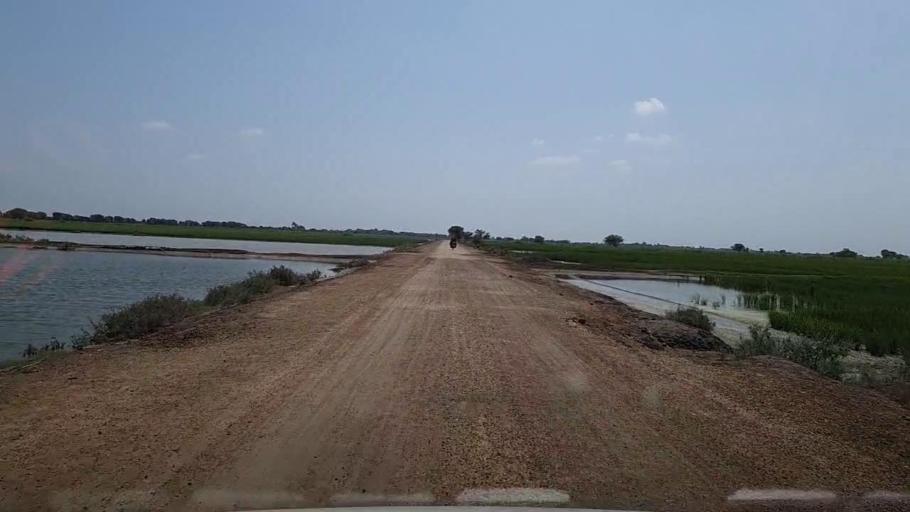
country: PK
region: Sindh
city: Kario
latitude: 24.8387
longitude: 68.7029
